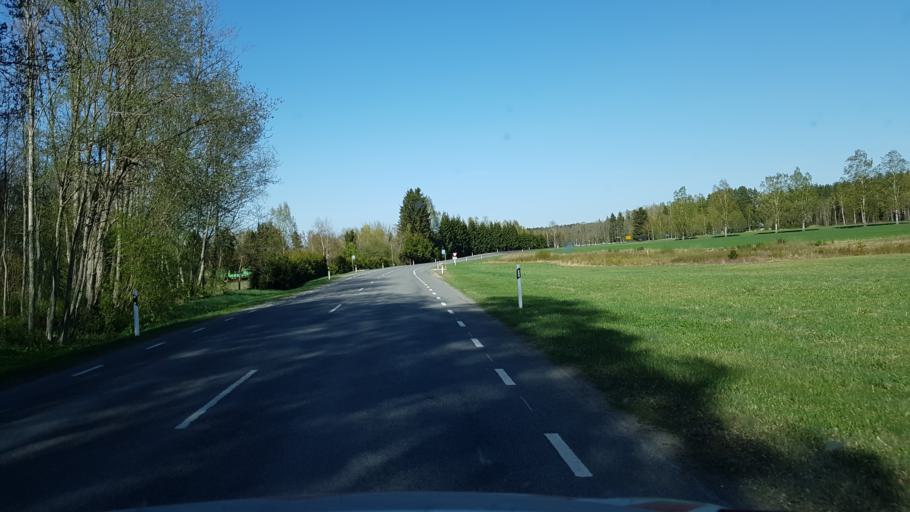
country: EE
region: Viljandimaa
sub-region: Viljandi linn
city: Viljandi
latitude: 58.3199
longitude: 25.5698
